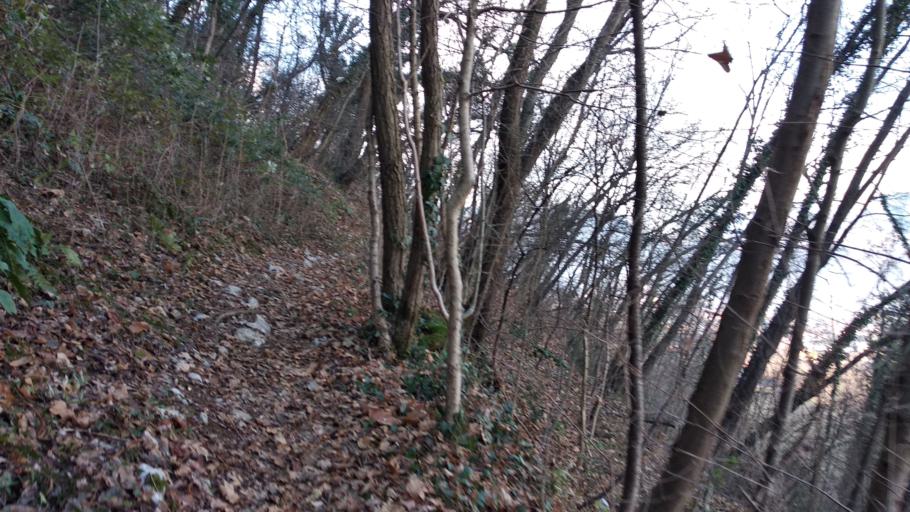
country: IT
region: Veneto
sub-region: Provincia di Vicenza
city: Schio
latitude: 45.6973
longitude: 11.3550
